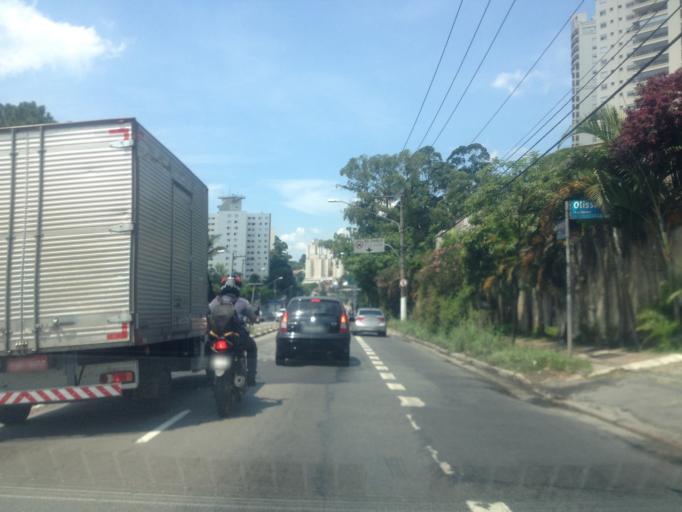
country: BR
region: Sao Paulo
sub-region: Diadema
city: Diadema
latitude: -23.6577
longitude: -46.6797
